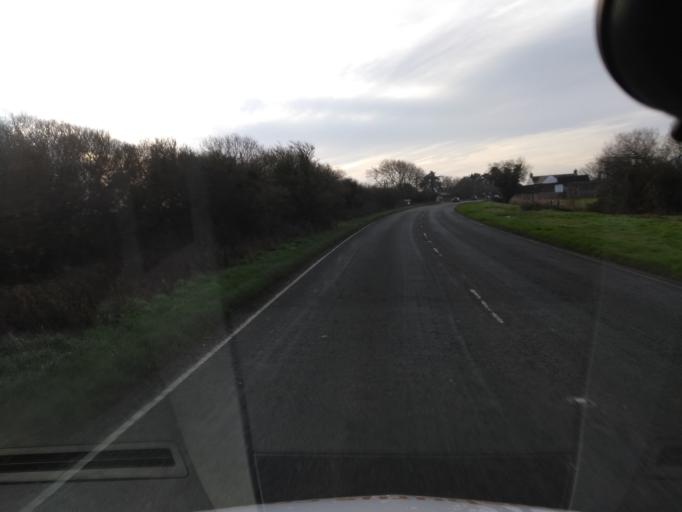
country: GB
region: England
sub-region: North Somerset
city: Bleadon
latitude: 51.2787
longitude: -2.9333
